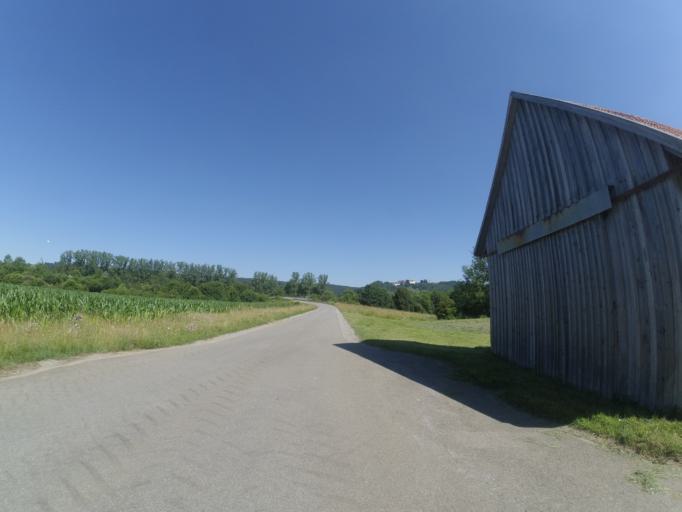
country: DE
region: Baden-Wuerttemberg
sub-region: Tuebingen Region
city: Leutkirch im Allgau
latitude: 47.8508
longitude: 9.9961
